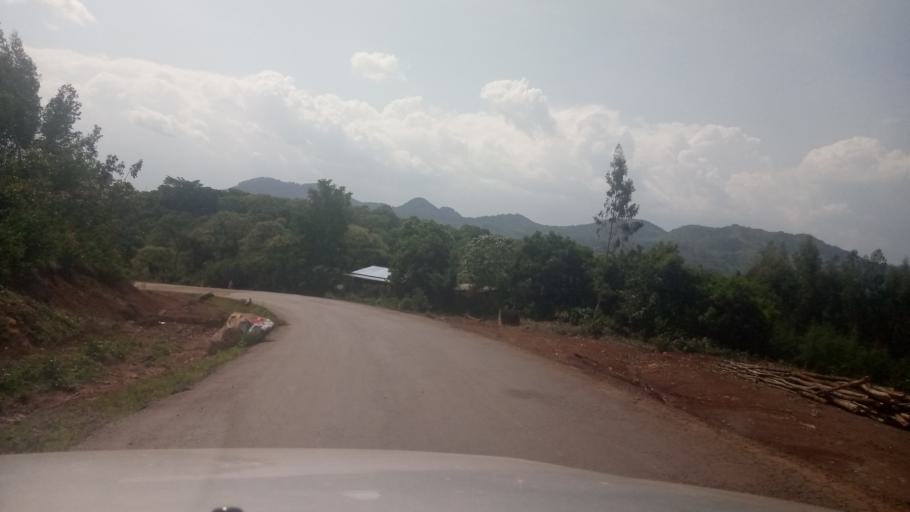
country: ET
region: Oromiya
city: Agaro
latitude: 7.9910
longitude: 36.5101
